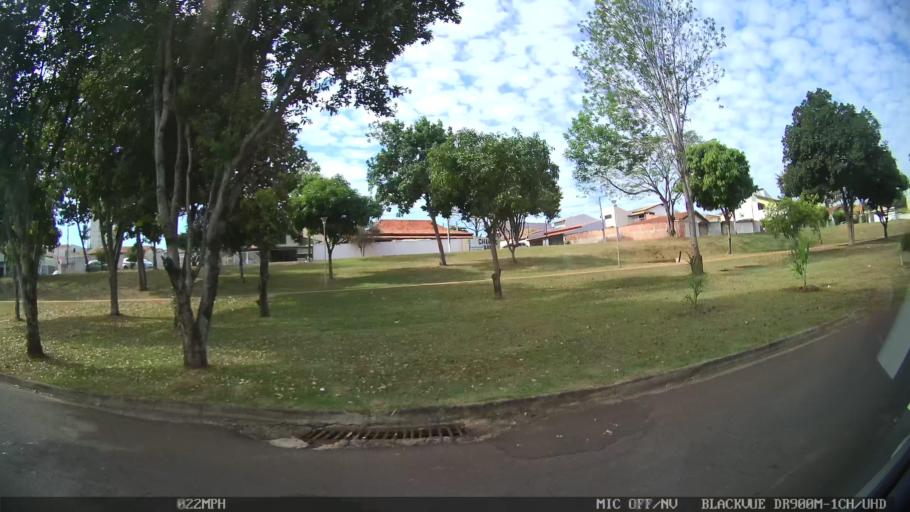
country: BR
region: Sao Paulo
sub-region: Santa Barbara D'Oeste
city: Santa Barbara d'Oeste
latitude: -22.7641
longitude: -47.4029
